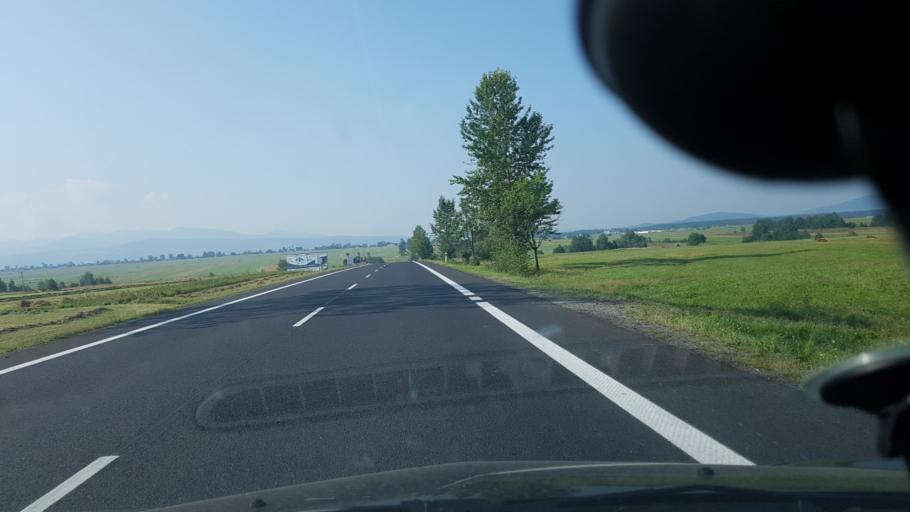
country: PL
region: Lesser Poland Voivodeship
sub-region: Powiat nowotarski
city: Chyzne
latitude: 49.4458
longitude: 19.6848
